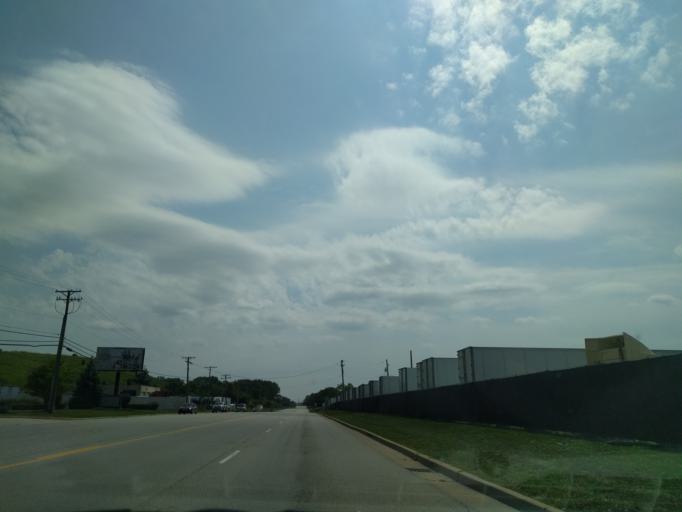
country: US
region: Illinois
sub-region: Cook County
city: Elk Grove Village
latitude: 42.0193
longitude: -87.9550
